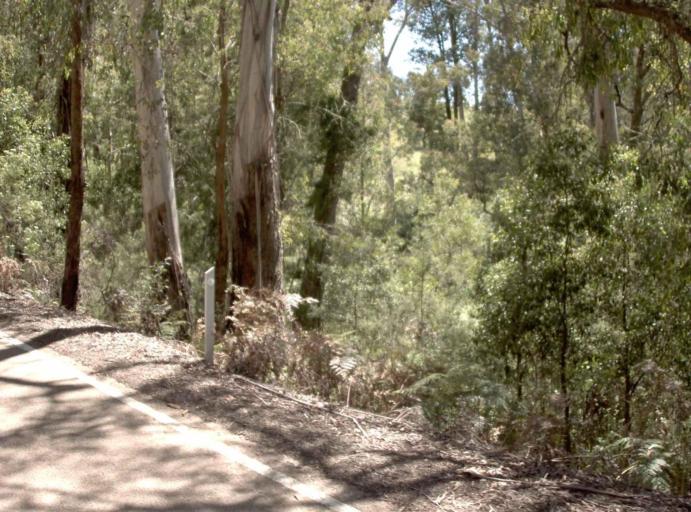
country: AU
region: Victoria
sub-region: East Gippsland
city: Lakes Entrance
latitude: -37.2241
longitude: 148.2636
